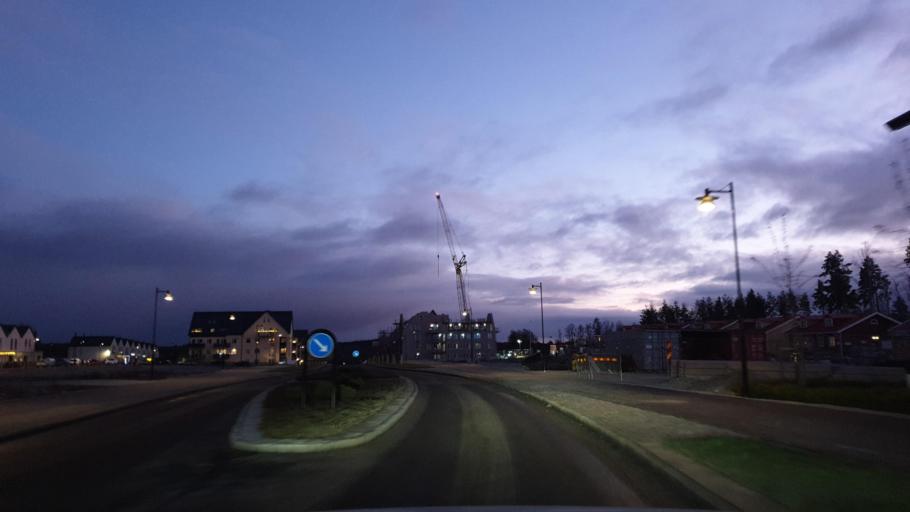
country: SE
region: Stockholm
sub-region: Sigtuna Kommun
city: Marsta
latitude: 59.6088
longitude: 17.7956
